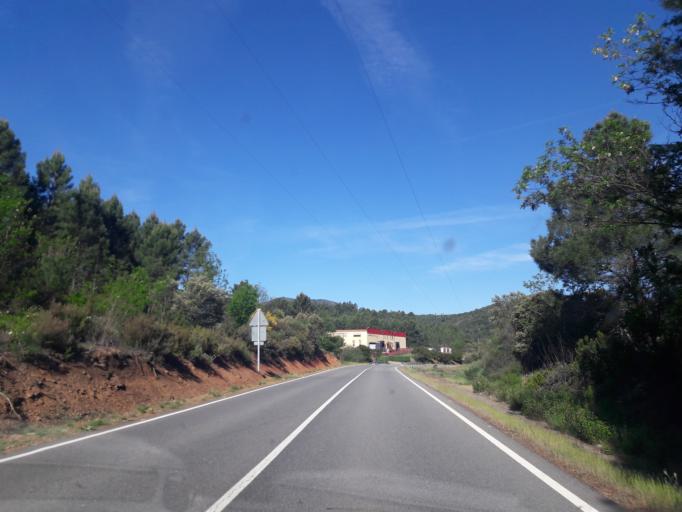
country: ES
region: Castille and Leon
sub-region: Provincia de Salamanca
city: Herguijuela de la Sierra
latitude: 40.4139
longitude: -6.1147
